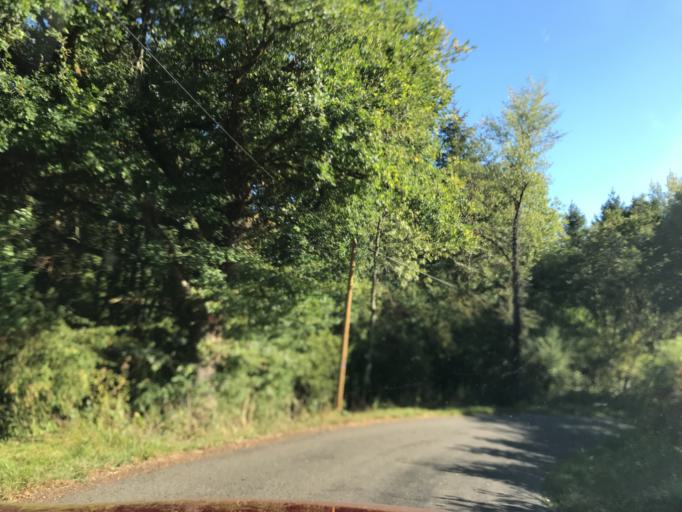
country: FR
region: Auvergne
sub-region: Departement du Puy-de-Dome
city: Escoutoux
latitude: 45.7867
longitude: 3.6077
